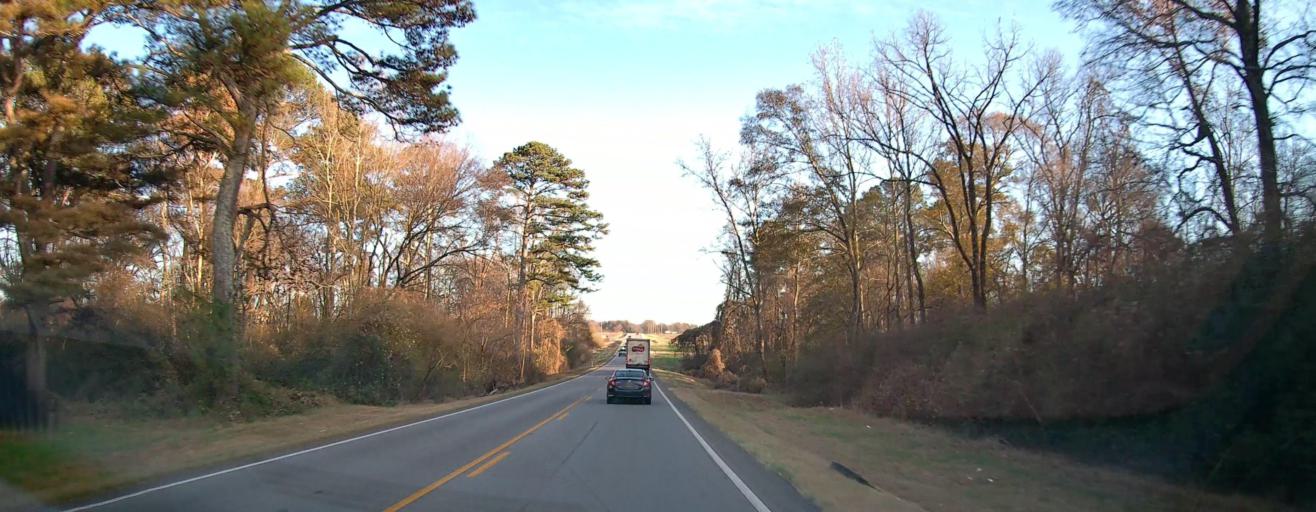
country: US
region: Alabama
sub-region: Blount County
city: Oneonta
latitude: 34.1020
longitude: -86.3679
